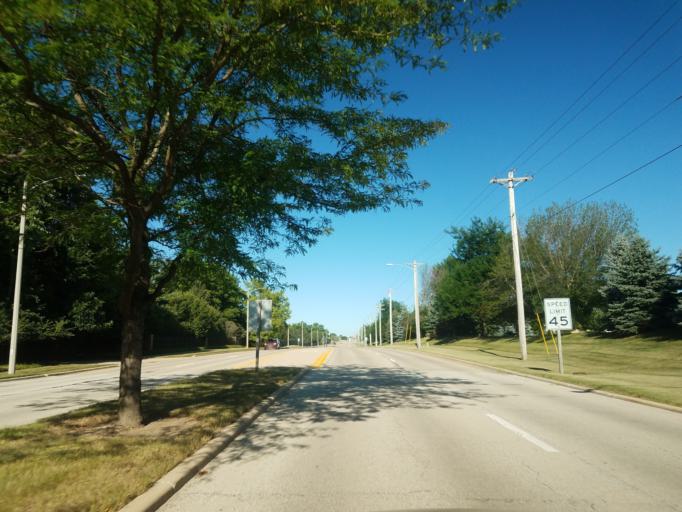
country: US
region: Illinois
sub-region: McLean County
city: Bloomington
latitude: 40.4588
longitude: -88.9381
